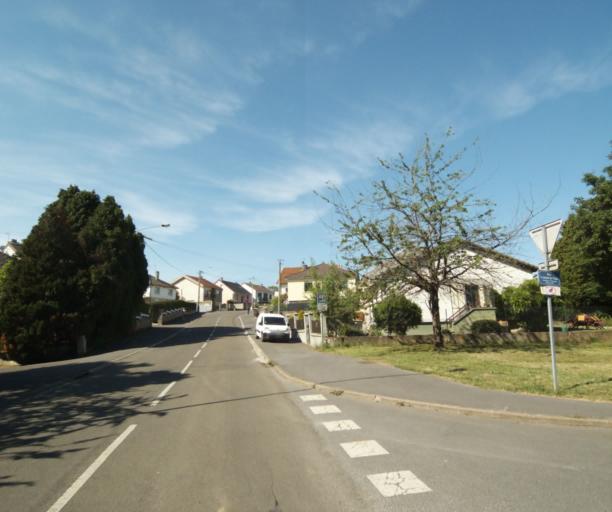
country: FR
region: Champagne-Ardenne
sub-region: Departement des Ardennes
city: Warcq
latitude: 49.7841
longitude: 4.6910
